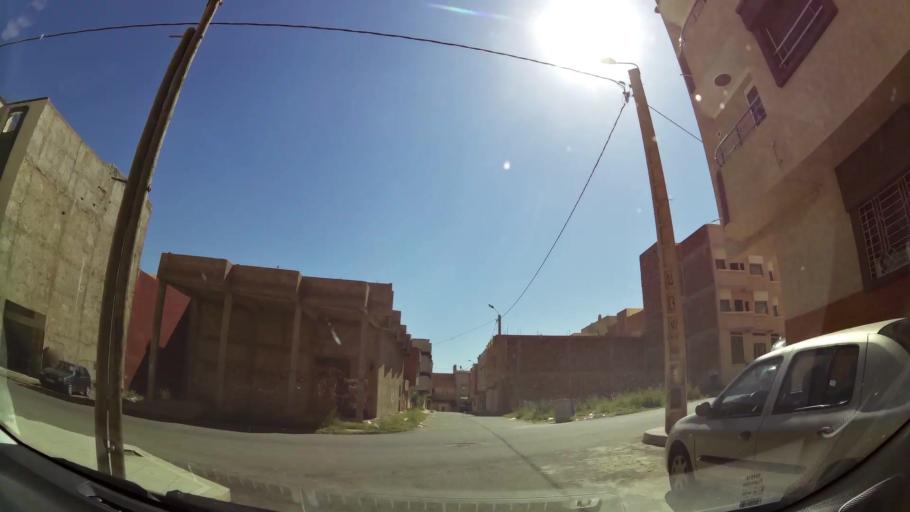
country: MA
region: Oriental
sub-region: Oujda-Angad
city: Oujda
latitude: 34.6561
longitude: -1.8886
